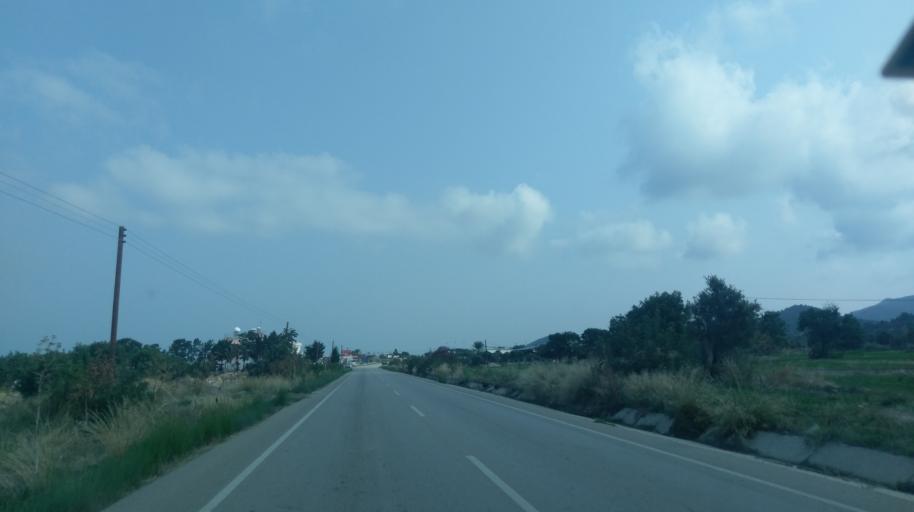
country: CY
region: Ammochostos
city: Lefkonoiko
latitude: 35.3912
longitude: 33.7409
